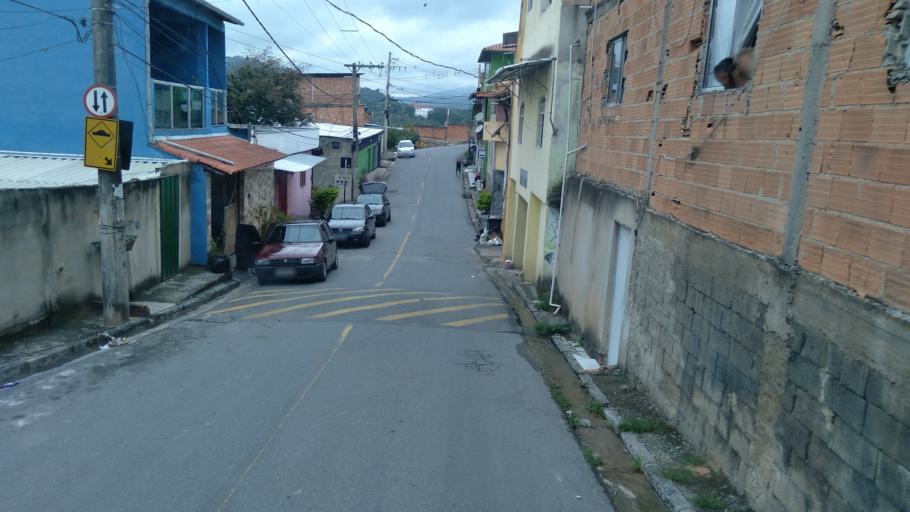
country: BR
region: Minas Gerais
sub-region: Santa Luzia
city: Santa Luzia
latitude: -19.8291
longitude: -43.8682
